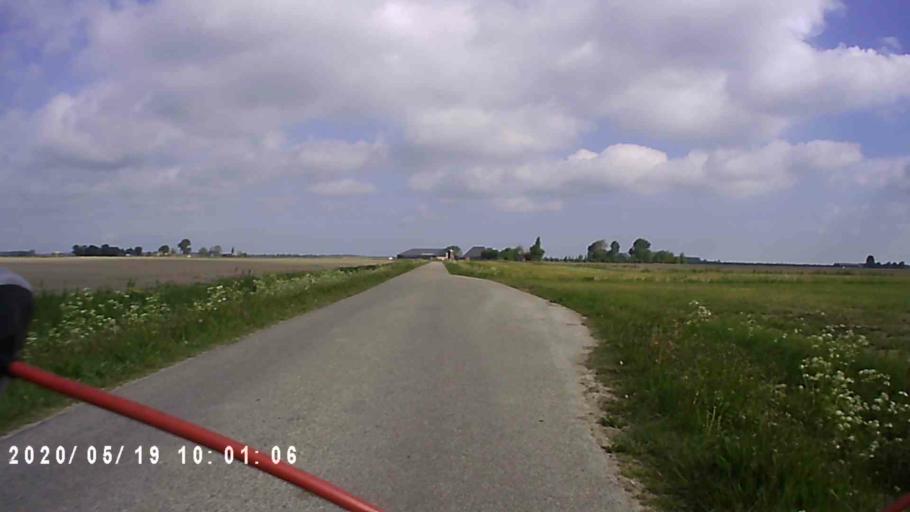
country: NL
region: Groningen
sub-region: Gemeente Zuidhorn
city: Grijpskerk
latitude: 53.3008
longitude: 6.2359
